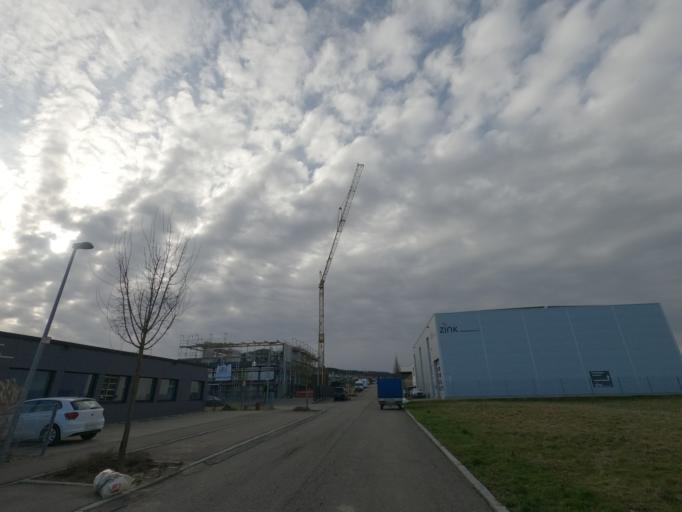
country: DE
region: Baden-Wuerttemberg
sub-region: Regierungsbezirk Stuttgart
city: Zell unter Aichelberg
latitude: 48.6479
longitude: 9.5623
